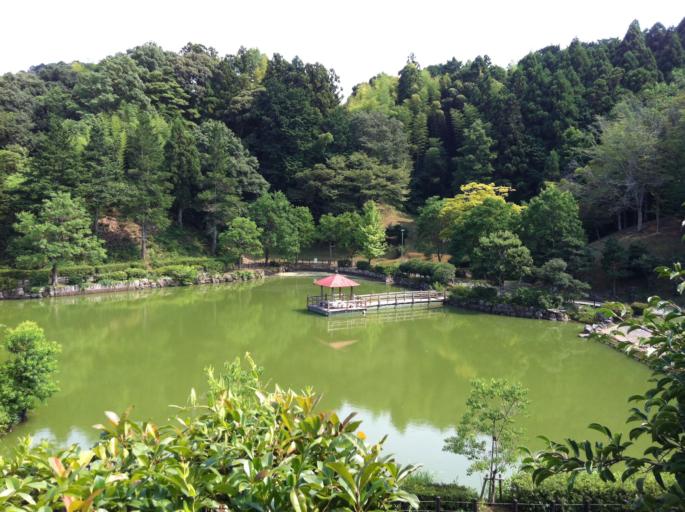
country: JP
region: Shizuoka
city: Shimada
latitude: 34.8497
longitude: 138.1740
